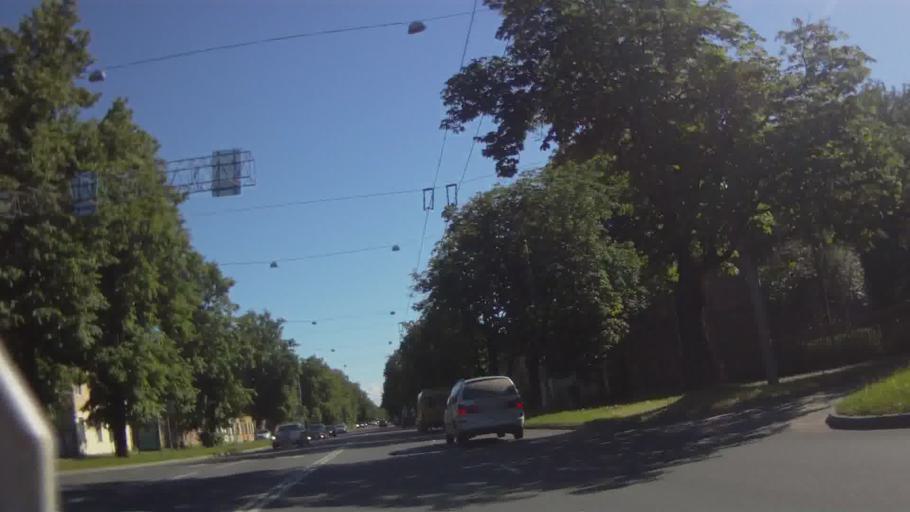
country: LV
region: Riga
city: Riga
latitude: 56.9179
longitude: 24.0882
